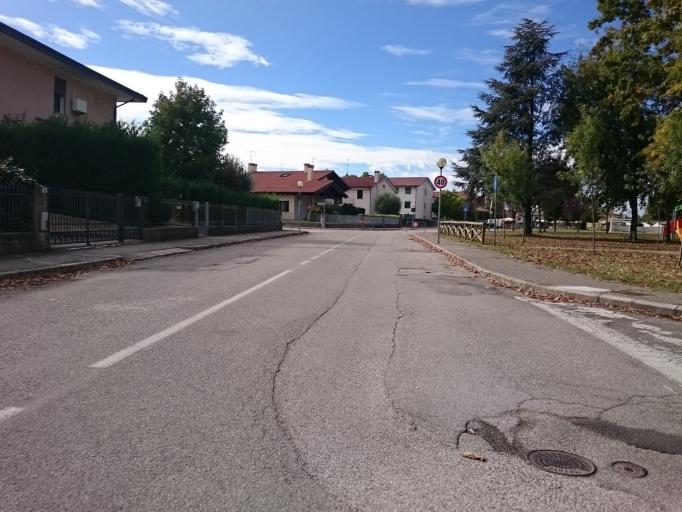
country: IT
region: Veneto
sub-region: Provincia di Padova
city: Bovolenta
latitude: 45.2667
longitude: 11.9371
